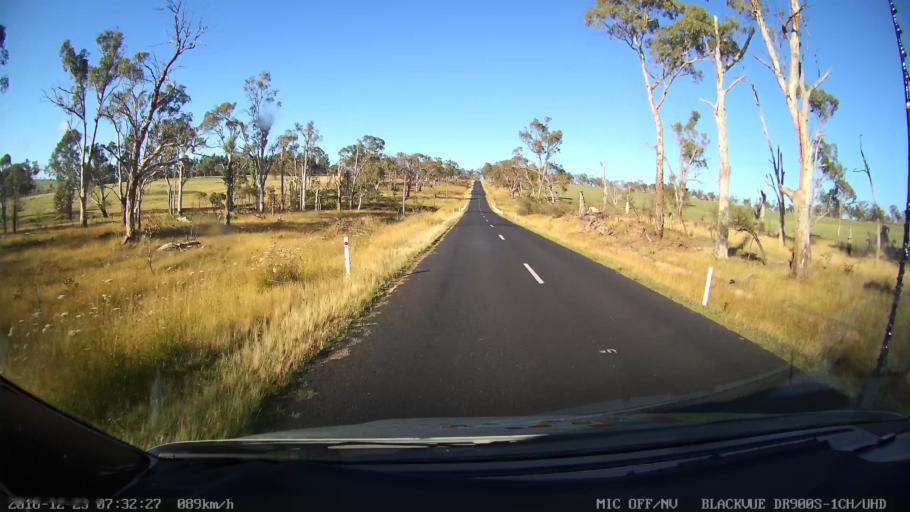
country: AU
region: New South Wales
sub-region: Armidale Dumaresq
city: Enmore
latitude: -30.5048
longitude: 152.1169
